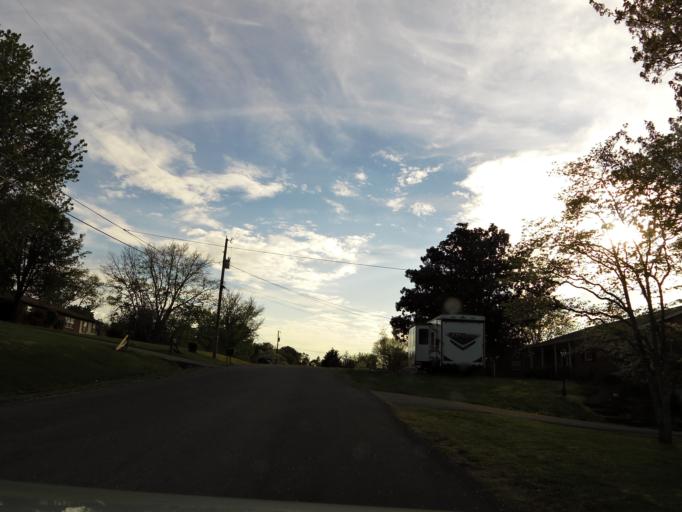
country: US
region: Tennessee
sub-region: Blount County
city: Maryville
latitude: 35.7039
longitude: -84.0166
